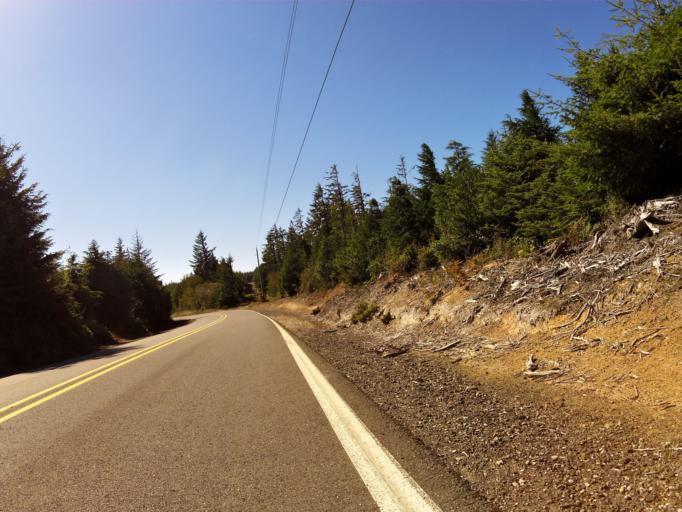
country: US
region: Oregon
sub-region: Coos County
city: Barview
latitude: 43.2761
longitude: -124.3554
